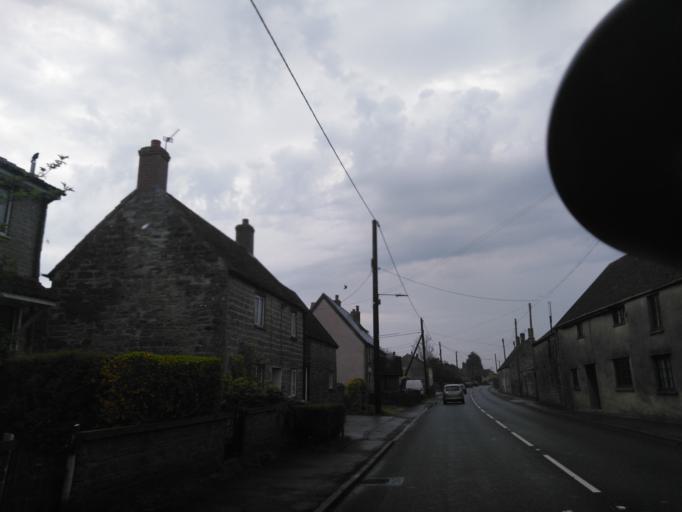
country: GB
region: England
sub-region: Somerset
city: Street
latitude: 51.1237
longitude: -2.7742
